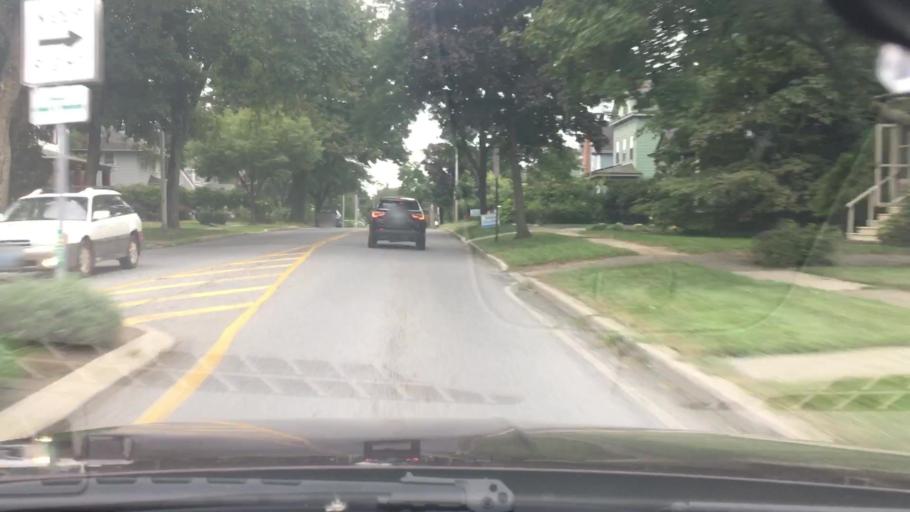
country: US
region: New York
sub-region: Dutchess County
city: Arlington
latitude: 41.6928
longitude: -73.9073
